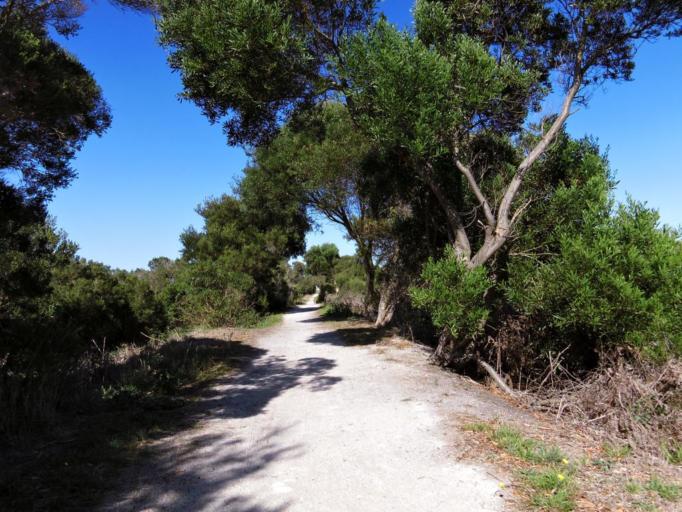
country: AU
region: Victoria
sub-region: Bass Coast
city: North Wonthaggi
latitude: -38.6145
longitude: 145.6004
